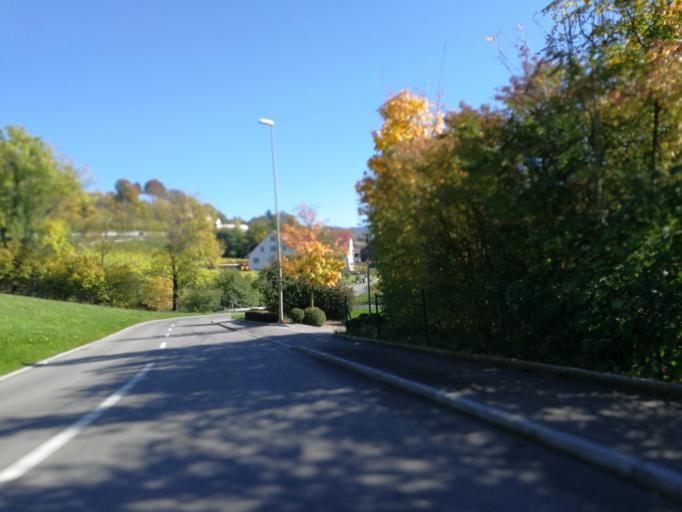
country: CH
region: Zurich
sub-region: Bezirk Meilen
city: Uetikon / Grossdorf
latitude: 47.2712
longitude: 8.6714
